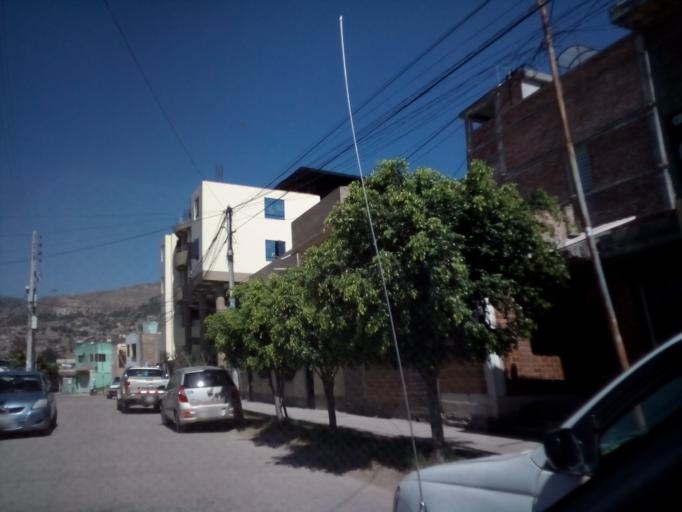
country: PE
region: Ayacucho
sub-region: Provincia de Huamanga
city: Ayacucho
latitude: -13.1480
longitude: -74.2239
